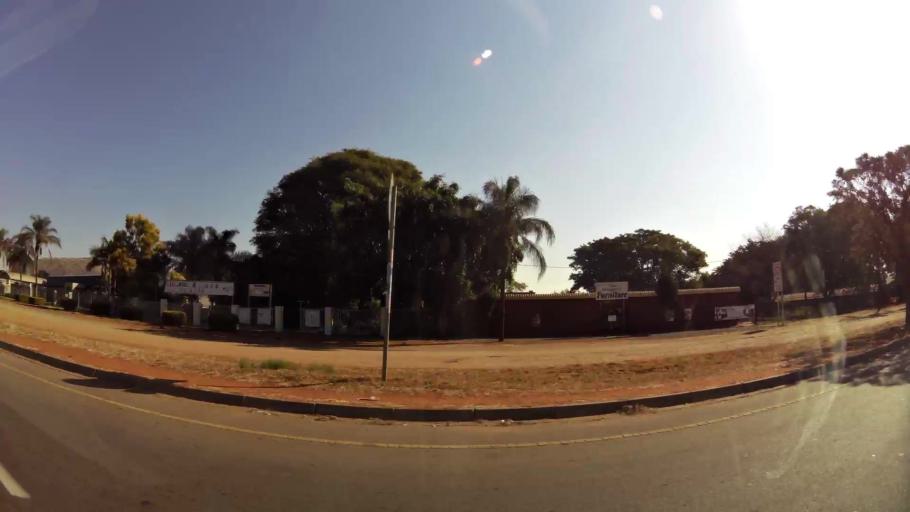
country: ZA
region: Gauteng
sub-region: City of Tshwane Metropolitan Municipality
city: Pretoria
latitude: -25.6753
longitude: 28.1946
